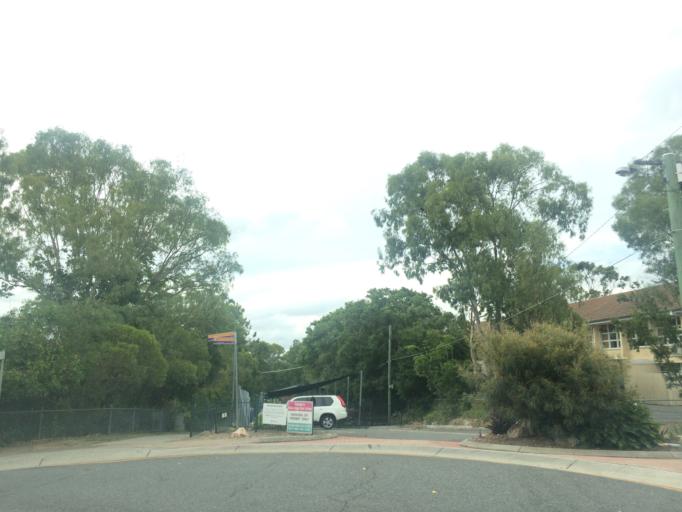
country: AU
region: Queensland
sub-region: Brisbane
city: Spring Hill
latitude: -27.4503
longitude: 153.0131
